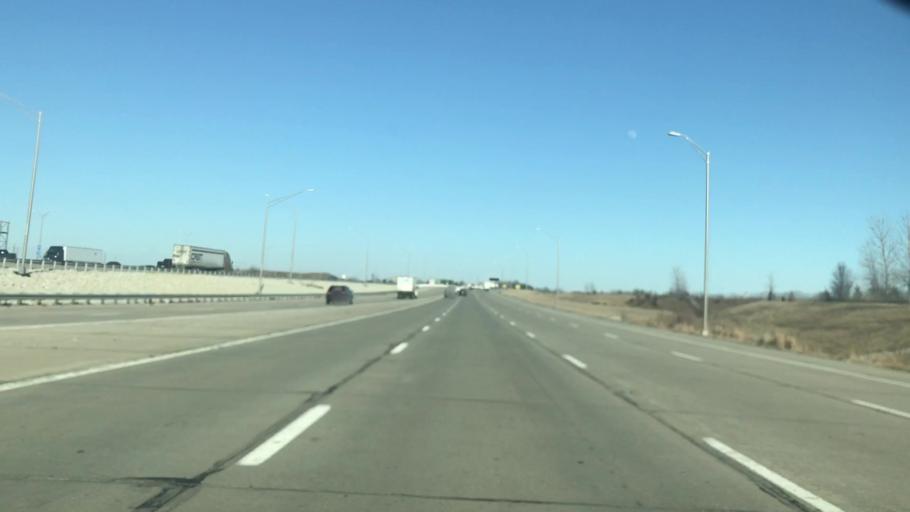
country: US
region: Indiana
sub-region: Hendricks County
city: Plainfield
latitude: 39.6925
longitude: -86.3094
